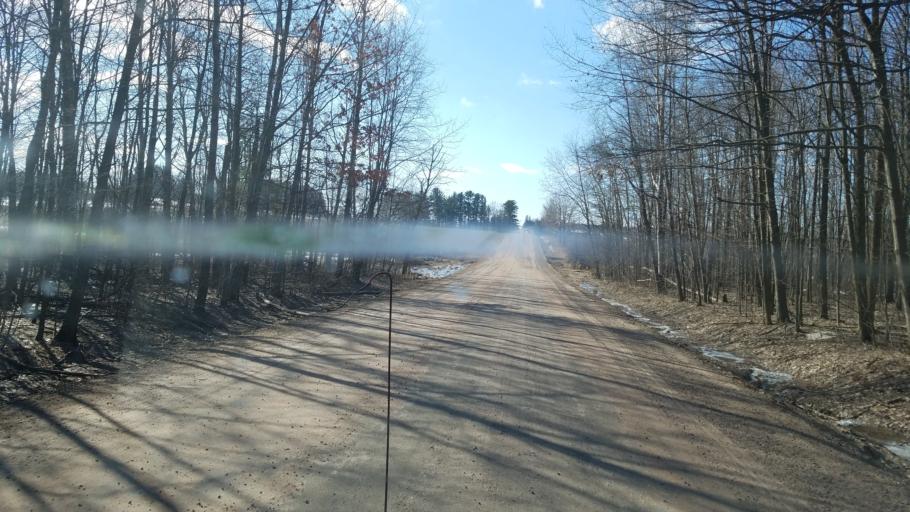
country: US
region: Wisconsin
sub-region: Clark County
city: Loyal
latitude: 44.6592
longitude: -90.4561
